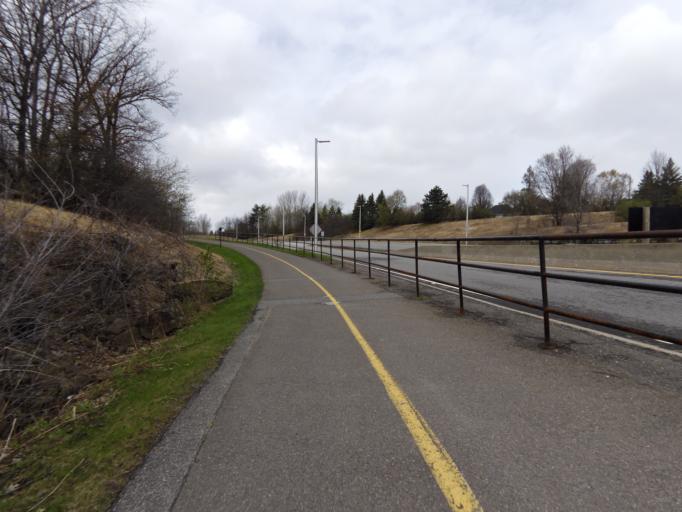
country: CA
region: Ontario
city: Bells Corners
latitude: 45.3600
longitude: -75.7738
